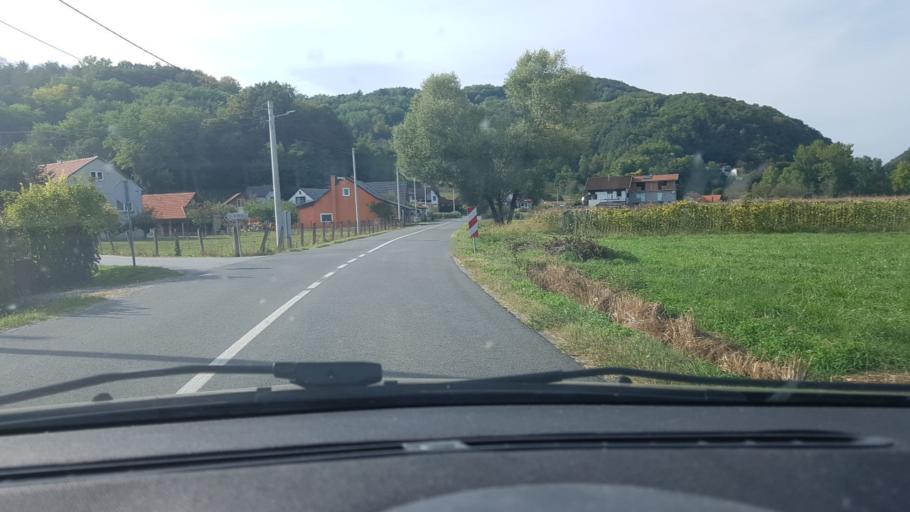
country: HR
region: Krapinsko-Zagorska
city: Mihovljan
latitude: 46.1062
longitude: 16.0141
